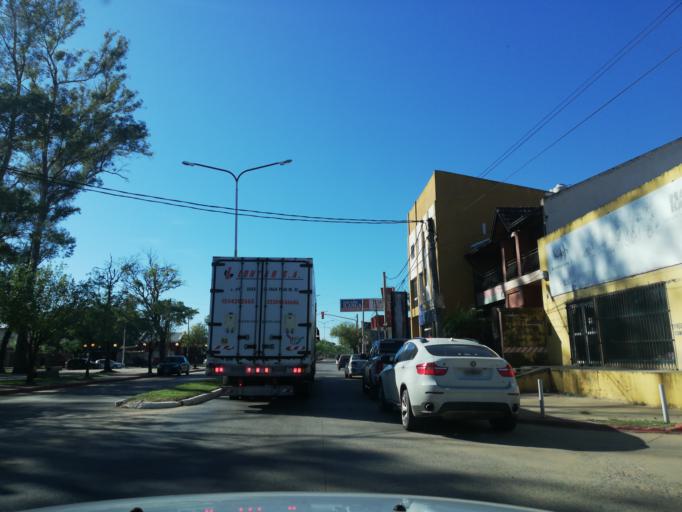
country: AR
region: Corrientes
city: Corrientes
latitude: -27.4766
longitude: -58.7894
